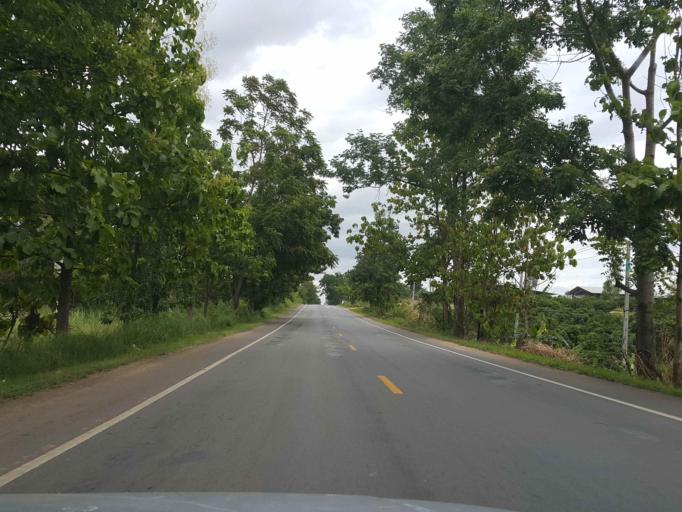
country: TH
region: Lamphun
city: Thung Hua Chang
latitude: 17.9776
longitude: 98.8764
